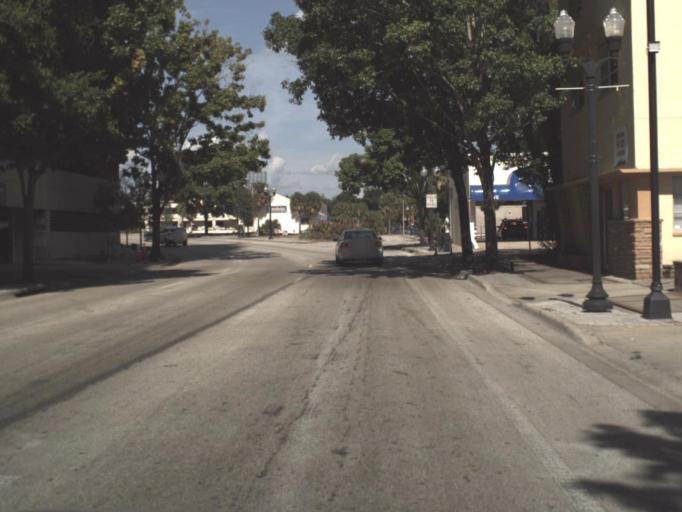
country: US
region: Florida
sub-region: Orange County
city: Orlando
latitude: 28.5459
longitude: -81.3759
